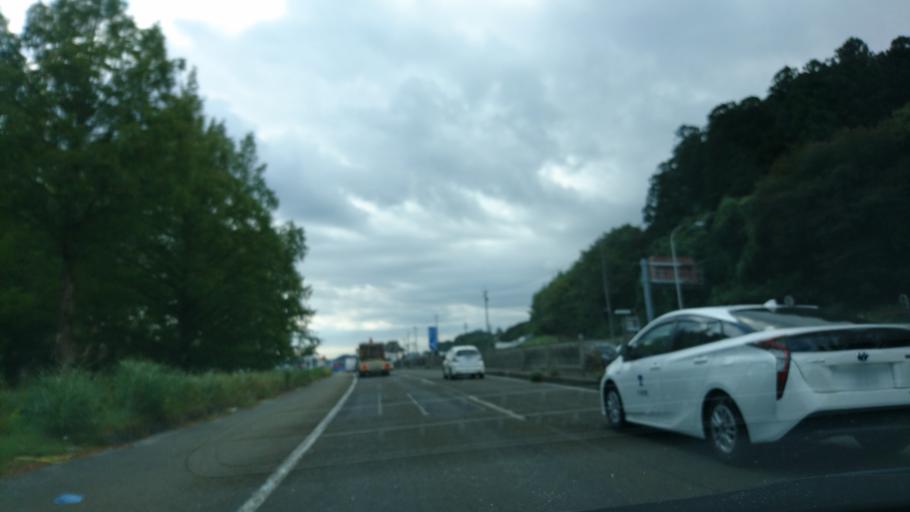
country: JP
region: Miyagi
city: Tomiya
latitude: 38.3438
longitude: 140.8801
